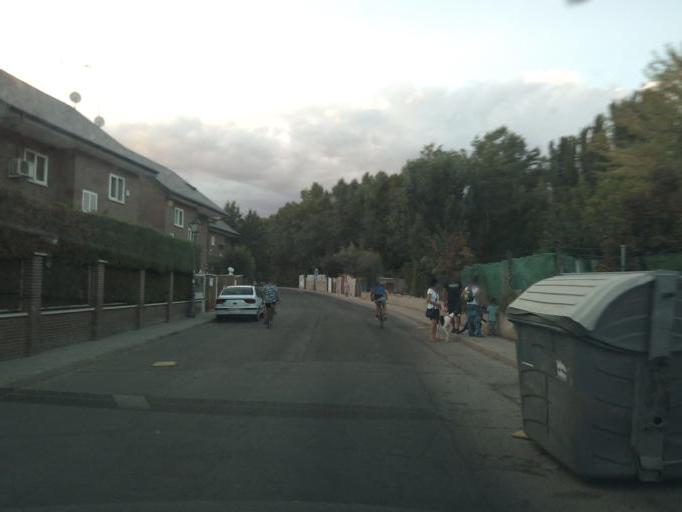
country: ES
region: Madrid
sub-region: Provincia de Madrid
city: Daganzo de Arriba
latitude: 40.5494
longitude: -3.4556
